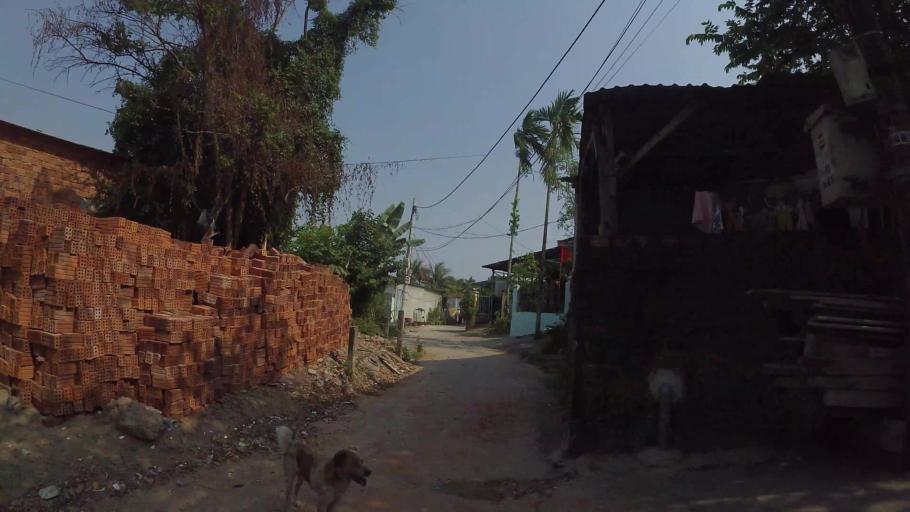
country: VN
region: Da Nang
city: Cam Le
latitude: 16.0121
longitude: 108.1943
